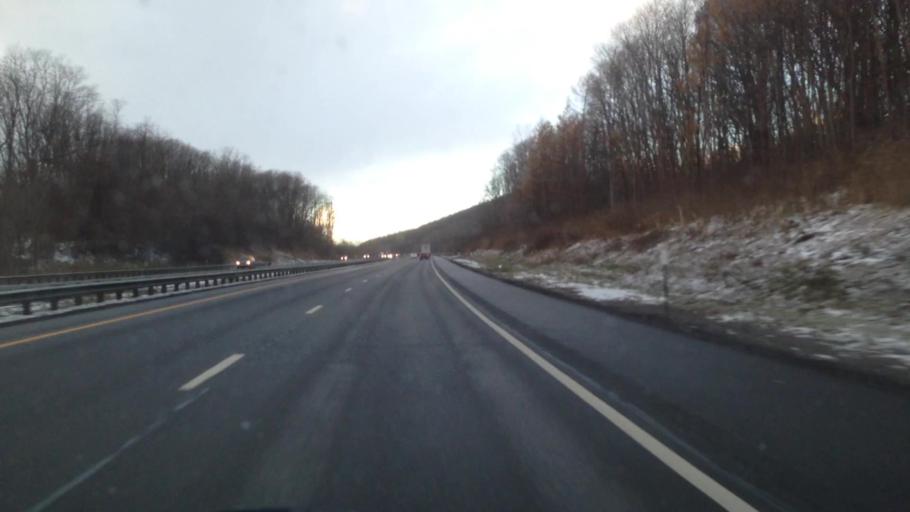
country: US
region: New York
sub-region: Herkimer County
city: Mohawk
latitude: 43.0197
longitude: -75.0151
